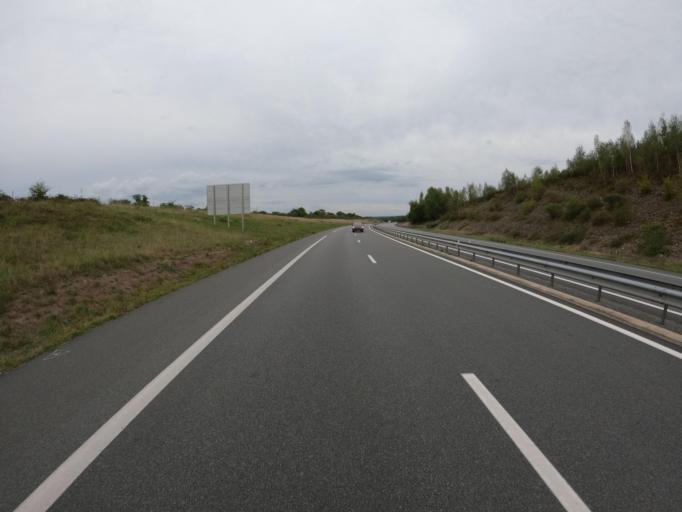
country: FR
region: Limousin
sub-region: Departement de la Creuse
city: Ajain
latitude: 46.2052
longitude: 2.0952
